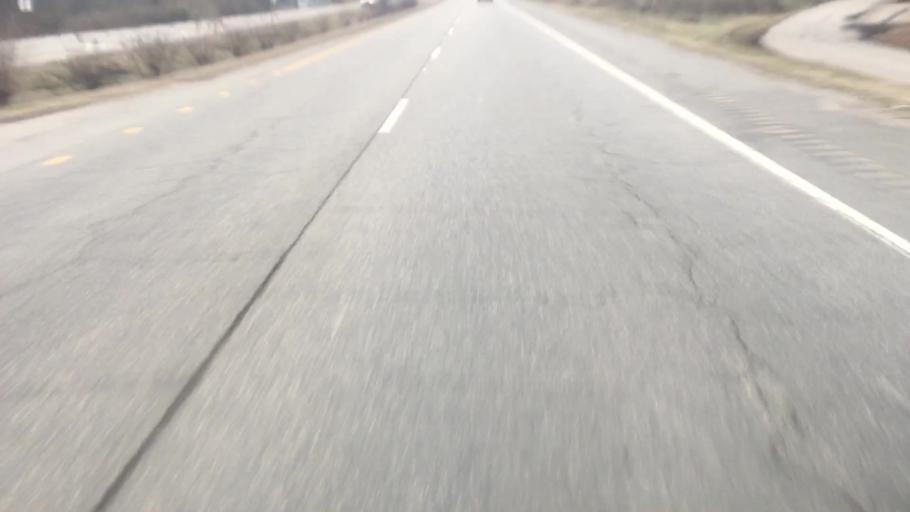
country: US
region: Alabama
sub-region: Walker County
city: Sumiton
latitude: 33.7406
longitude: -87.0354
